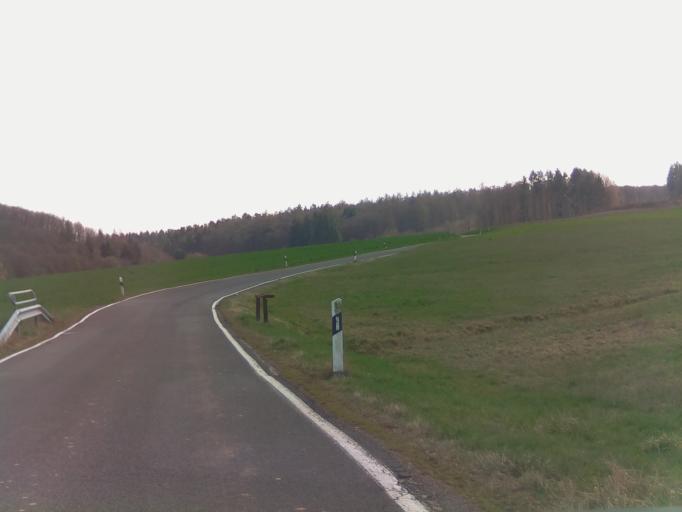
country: DE
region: Rheinland-Pfalz
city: Otzweiler
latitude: 49.7299
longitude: 7.5132
